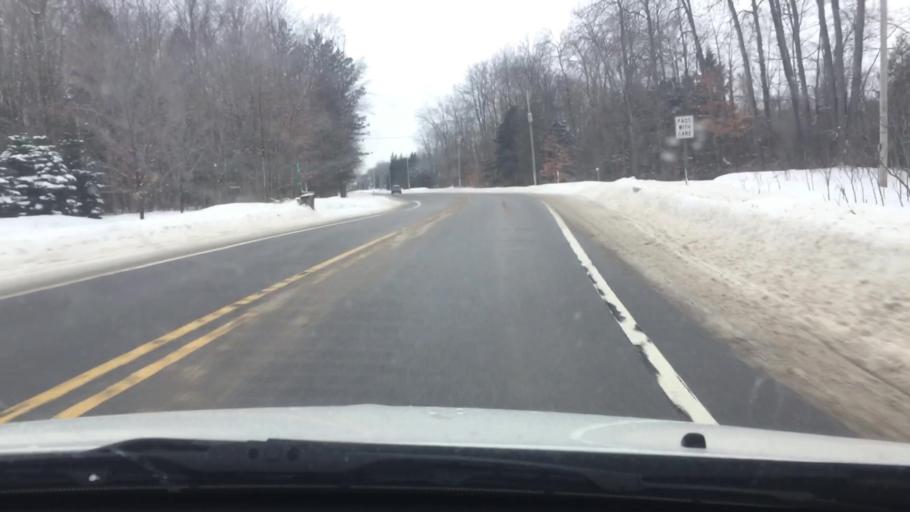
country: US
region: Michigan
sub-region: Charlevoix County
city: East Jordan
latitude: 45.1324
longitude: -85.0937
